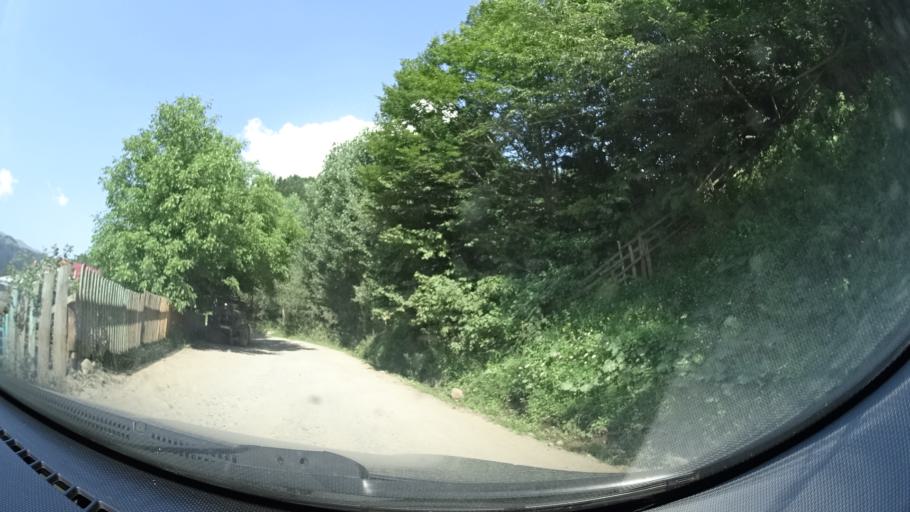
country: GE
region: Ajaria
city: Dioknisi
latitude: 41.6495
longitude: 42.4592
